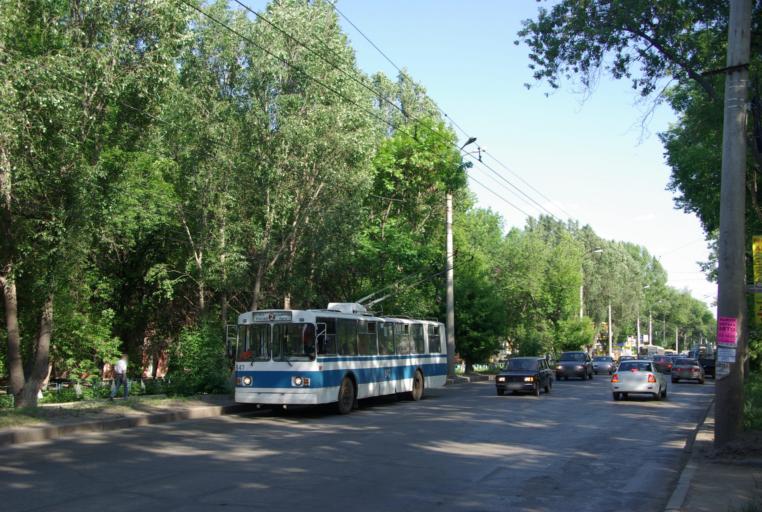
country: RU
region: Samara
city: Samara
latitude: 53.2350
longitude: 50.2426
